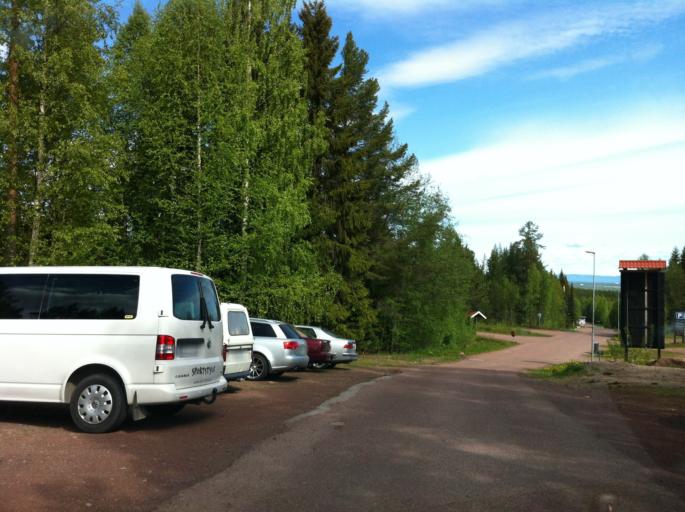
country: SE
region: Dalarna
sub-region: Mora Kommun
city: Mora
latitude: 60.8775
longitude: 14.5185
